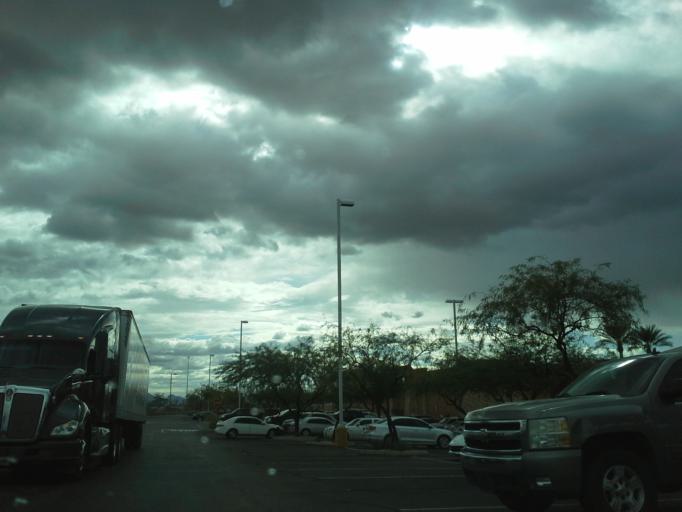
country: US
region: Arizona
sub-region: Maricopa County
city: Paradise Valley
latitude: 33.6750
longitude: -111.9701
